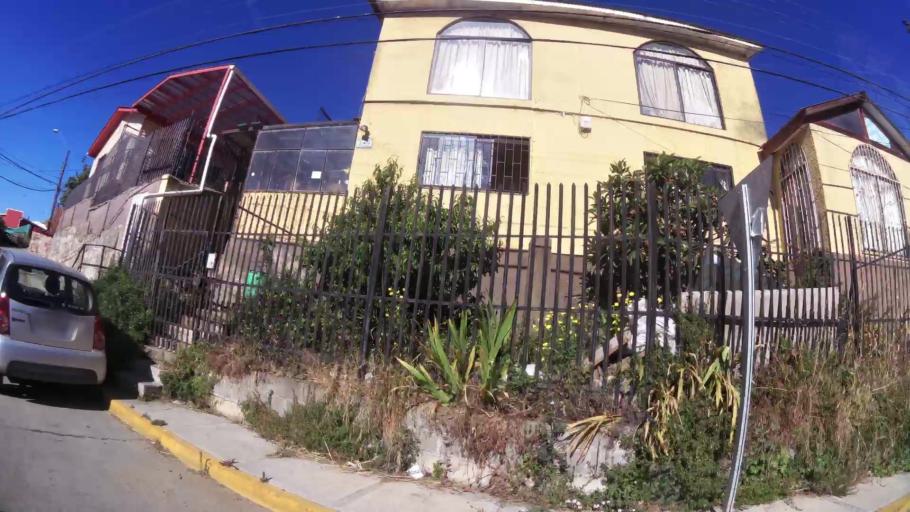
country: CL
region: Valparaiso
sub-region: Provincia de Valparaiso
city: Valparaiso
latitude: -33.0548
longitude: -71.6201
